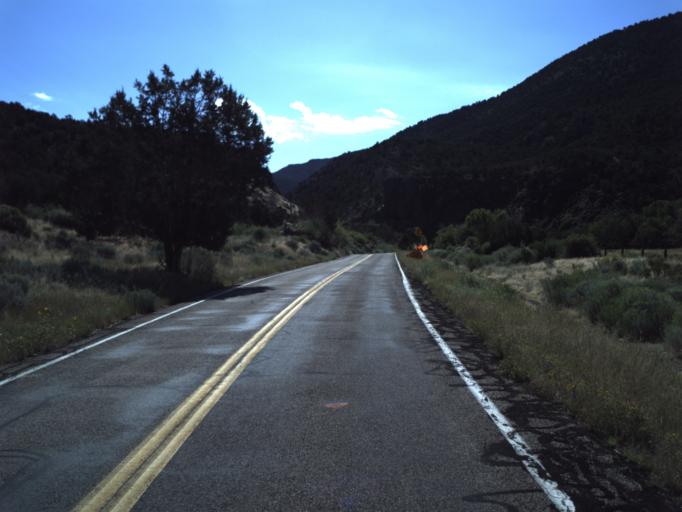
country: US
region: Utah
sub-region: Beaver County
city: Beaver
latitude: 38.2826
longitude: -112.5818
